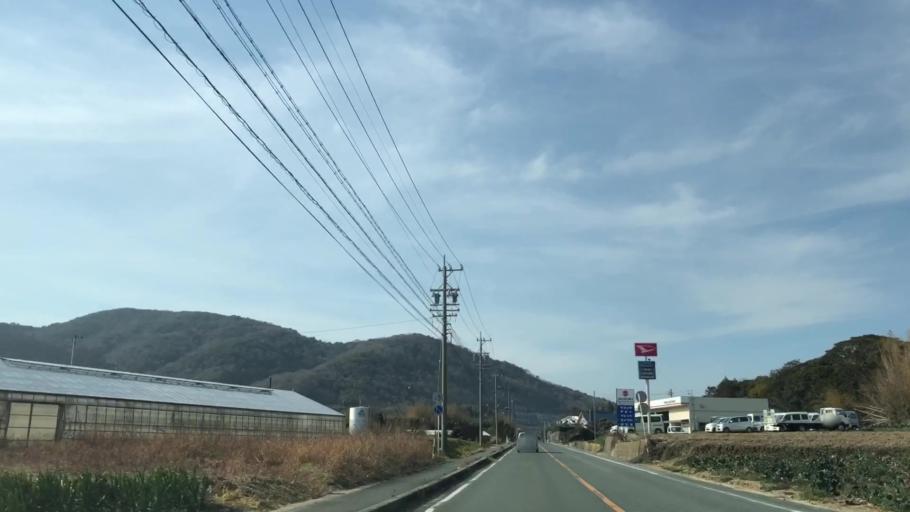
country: JP
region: Aichi
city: Tahara
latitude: 34.6769
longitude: 137.2535
